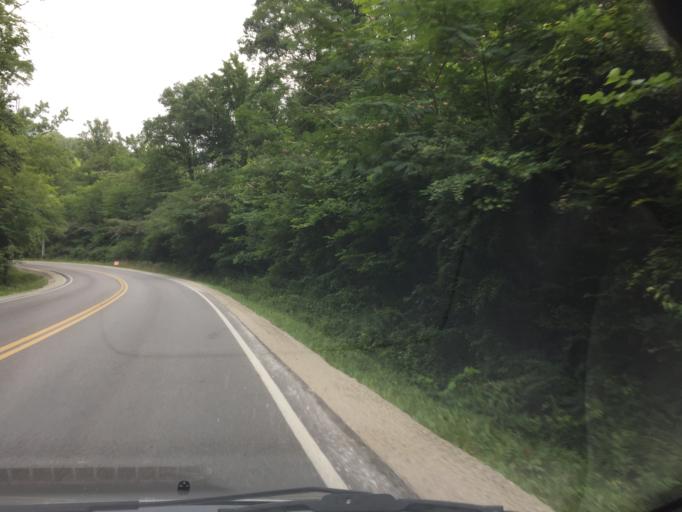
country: US
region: Tennessee
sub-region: Hamilton County
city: Apison
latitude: 34.9921
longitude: -85.0757
